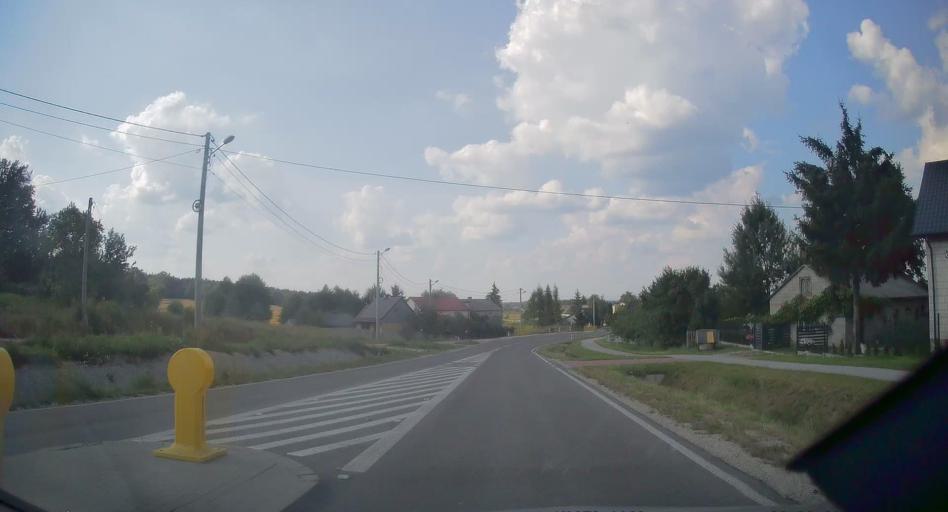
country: PL
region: Swietokrzyskie
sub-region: Powiat konecki
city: Radoszyce
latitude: 51.0386
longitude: 20.2833
